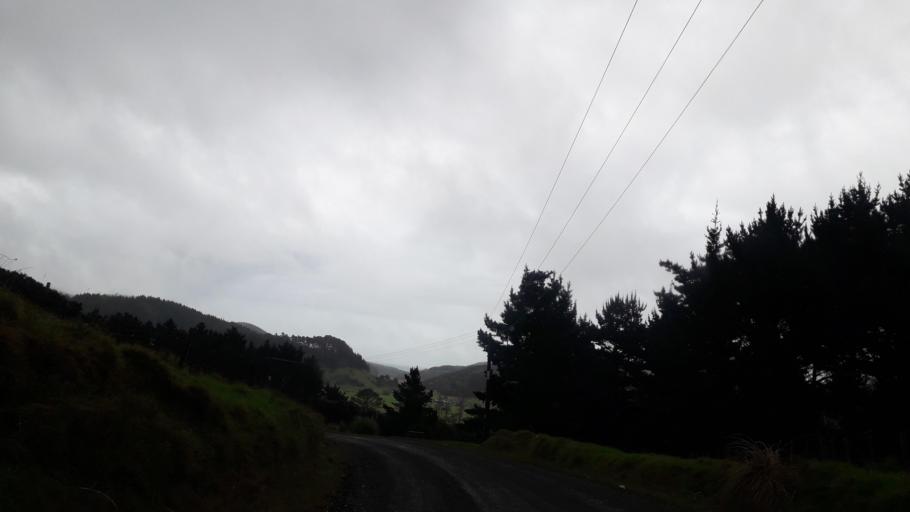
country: NZ
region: Northland
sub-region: Far North District
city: Ahipara
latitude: -35.4337
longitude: 173.3327
